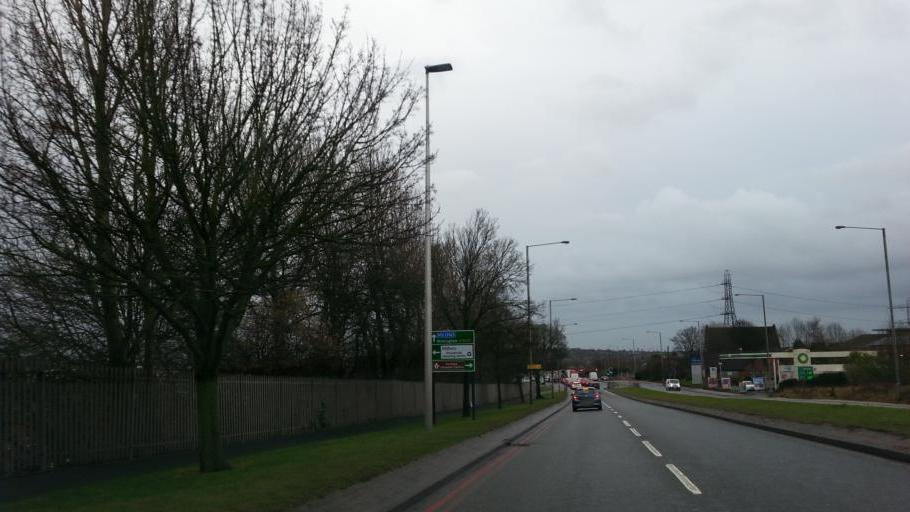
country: GB
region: England
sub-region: Sandwell
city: Oldbury
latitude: 52.5013
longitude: -2.0307
